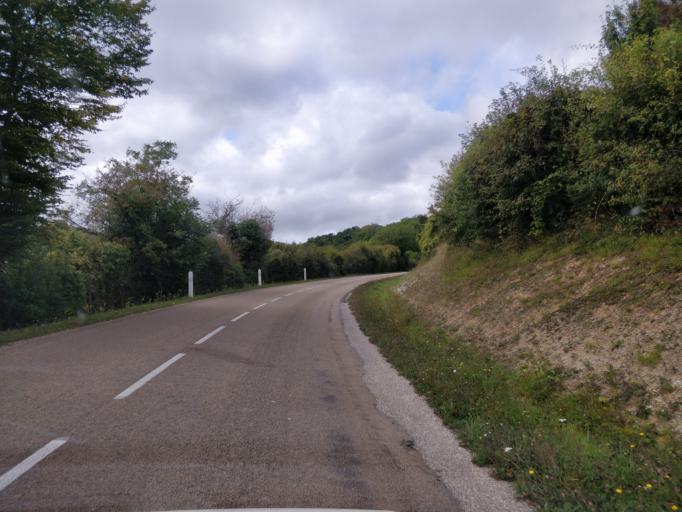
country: FR
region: Bourgogne
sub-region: Departement de l'Yonne
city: Saint-Florentin
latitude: 48.0948
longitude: 3.6864
